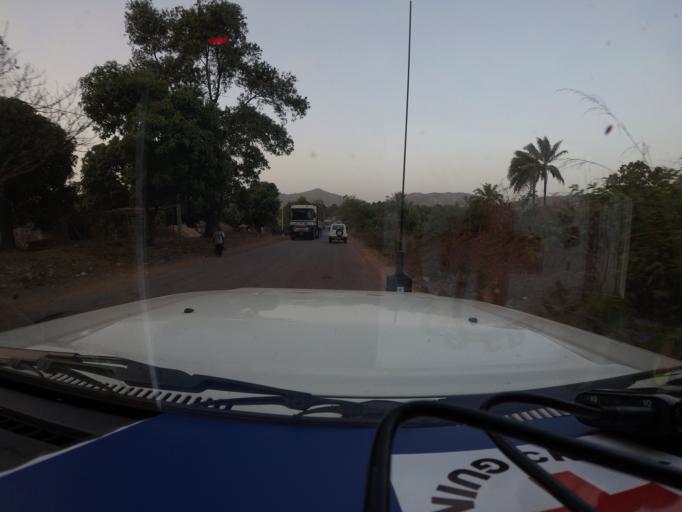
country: GN
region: Kindia
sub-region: Kindia
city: Kindia
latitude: 9.8584
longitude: -13.0825
